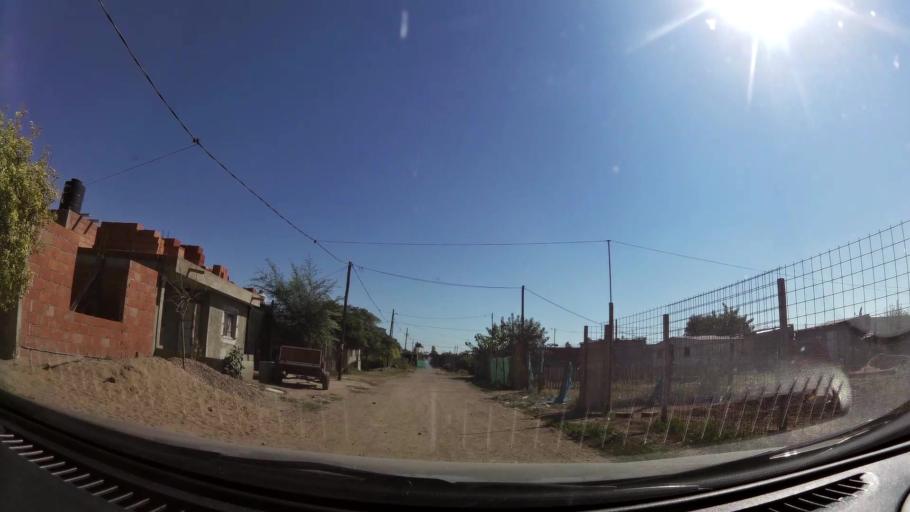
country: AR
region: Cordoba
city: Villa Allende
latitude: -31.3101
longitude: -64.2530
